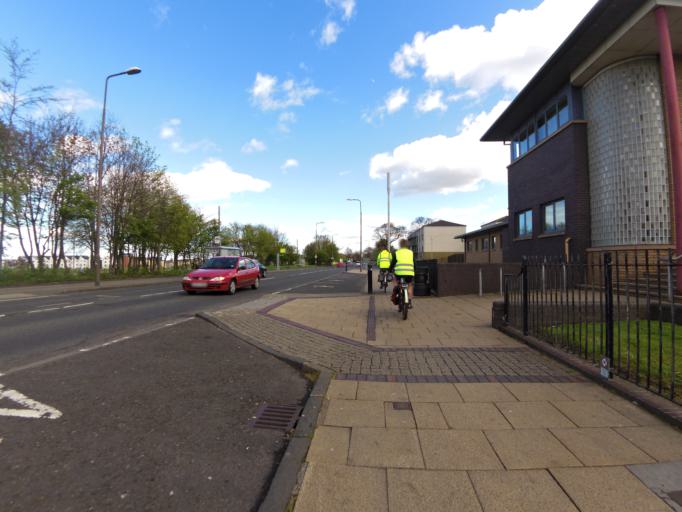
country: GB
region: Scotland
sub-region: West Lothian
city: Seafield
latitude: 55.9326
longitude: -3.1349
